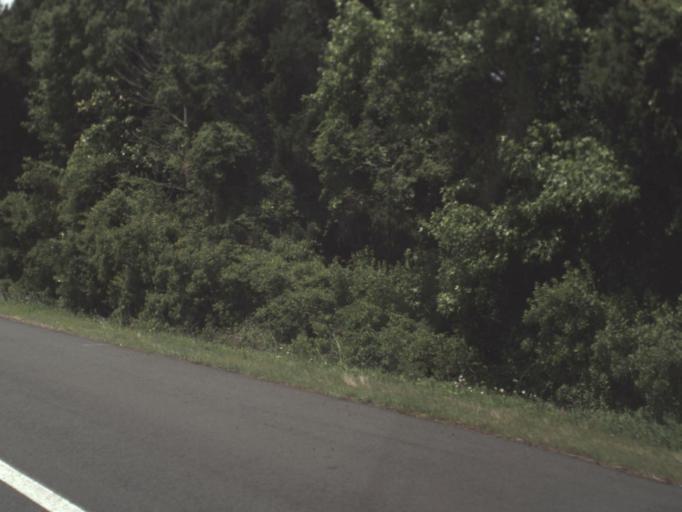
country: US
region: Georgia
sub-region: Camden County
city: Kingsland
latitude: 30.7332
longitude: -81.6602
